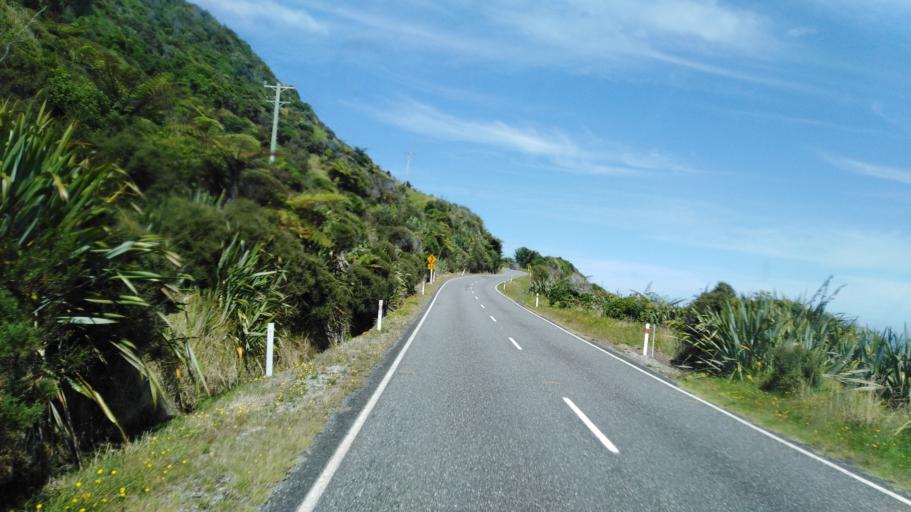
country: NZ
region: West Coast
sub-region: Buller District
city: Westport
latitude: -41.5699
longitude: 171.9072
